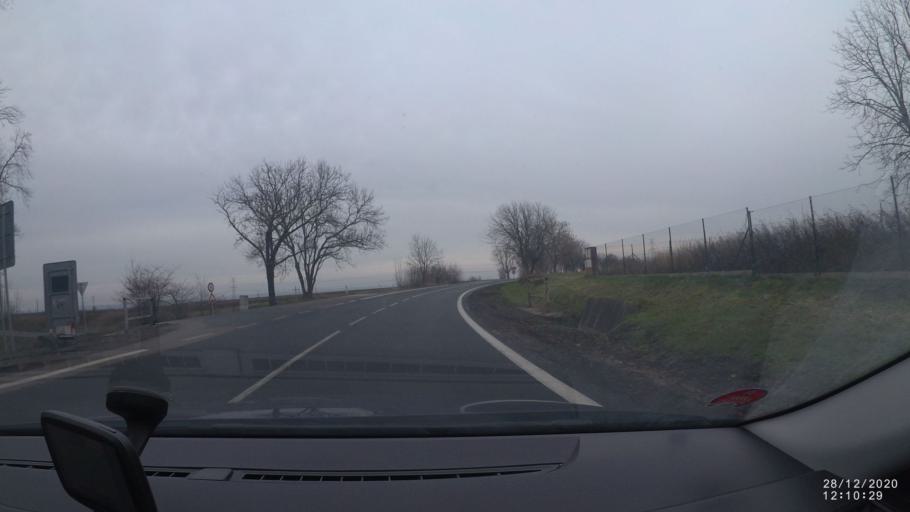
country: CZ
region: Central Bohemia
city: Brandys nad Labem-Stara Boleslav
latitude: 50.1693
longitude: 14.6319
